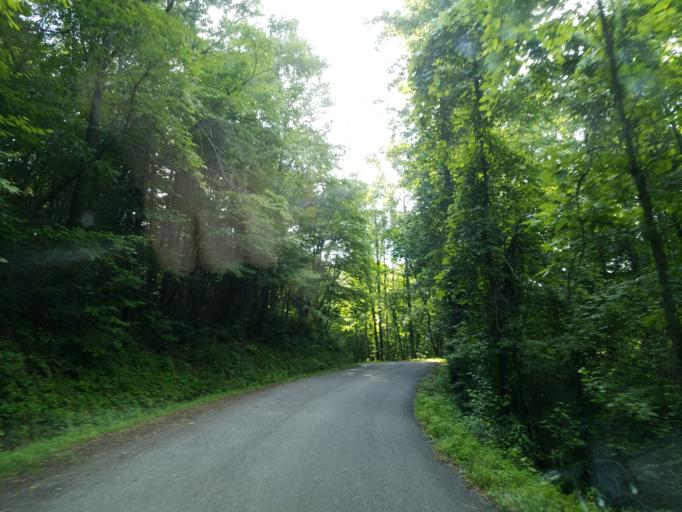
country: US
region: Georgia
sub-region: Gilmer County
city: Ellijay
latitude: 34.6313
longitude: -84.2639
